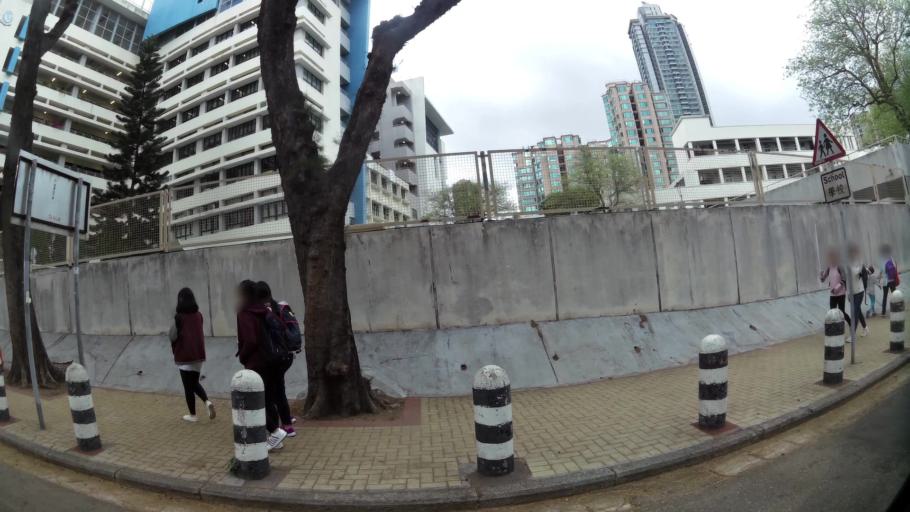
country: HK
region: Kowloon City
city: Kowloon
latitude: 22.3215
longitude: 114.1850
